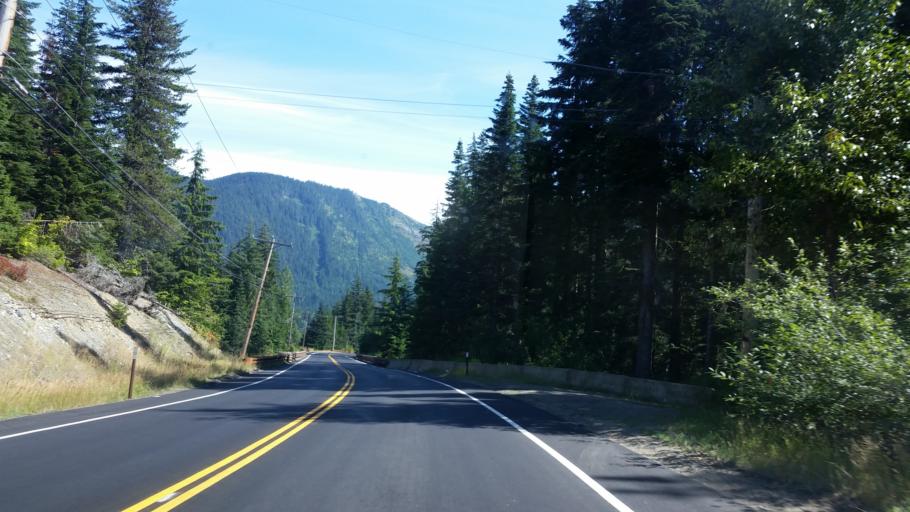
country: US
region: Washington
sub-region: King County
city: Tanner
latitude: 47.4013
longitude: -121.4058
